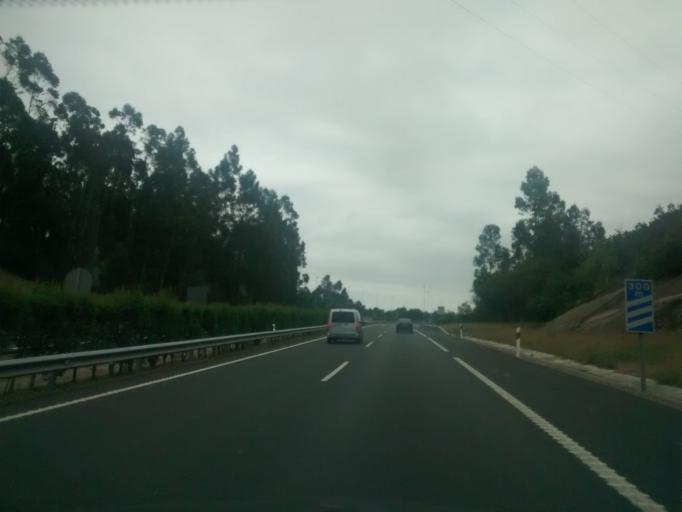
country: ES
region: Cantabria
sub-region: Provincia de Cantabria
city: Reocin
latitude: 43.3422
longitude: -4.1445
